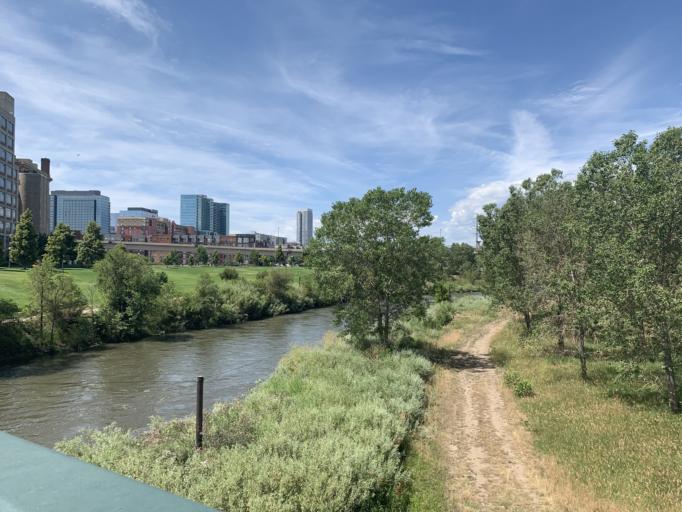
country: US
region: Colorado
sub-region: Denver County
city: Denver
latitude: 39.7619
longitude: -104.9999
